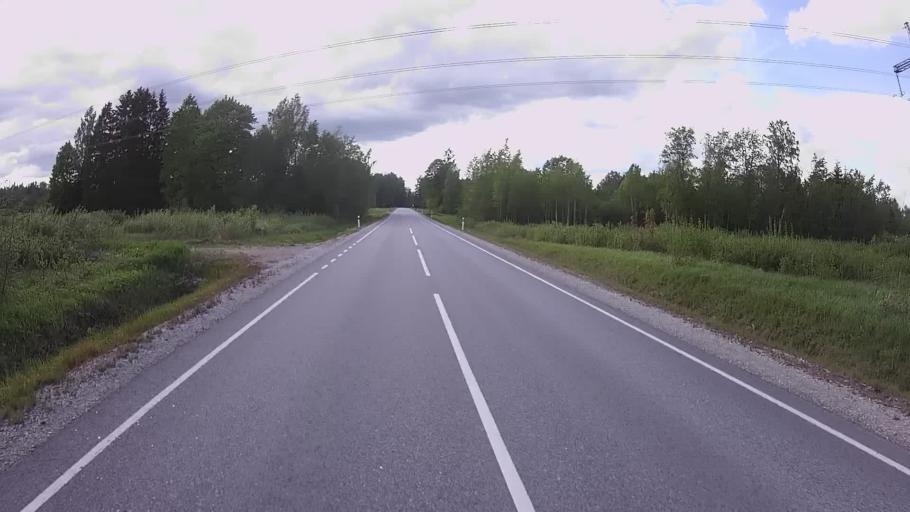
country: EE
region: Jogevamaa
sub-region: Mustvee linn
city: Mustvee
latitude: 58.8678
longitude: 26.8340
